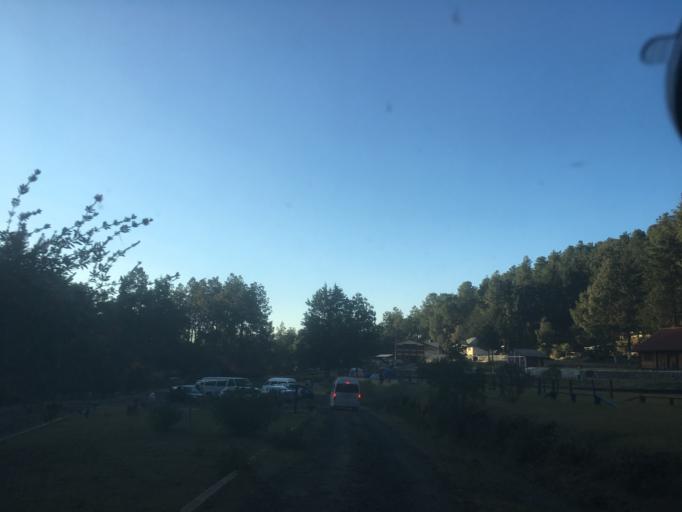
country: MX
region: Michoacan
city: Angahuan
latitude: 19.4935
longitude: -102.1990
